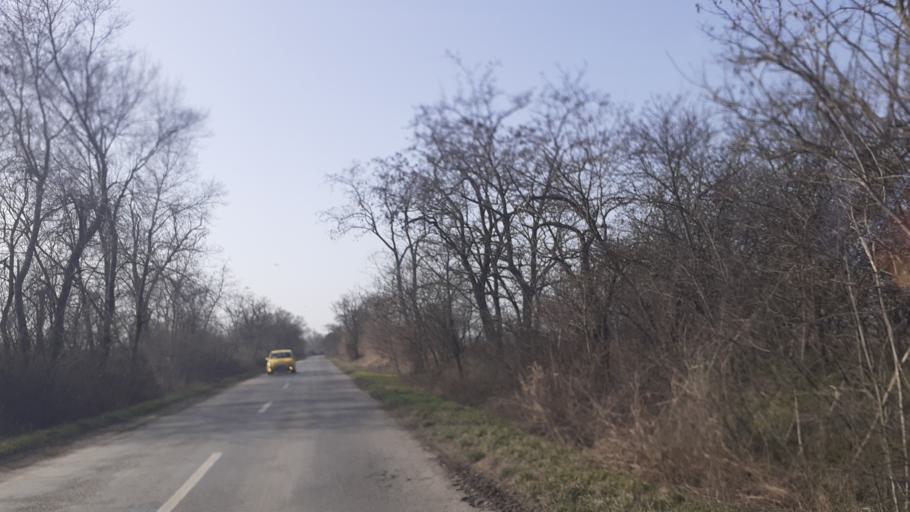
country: HU
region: Bacs-Kiskun
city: Tass
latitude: 47.0205
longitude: 18.9984
